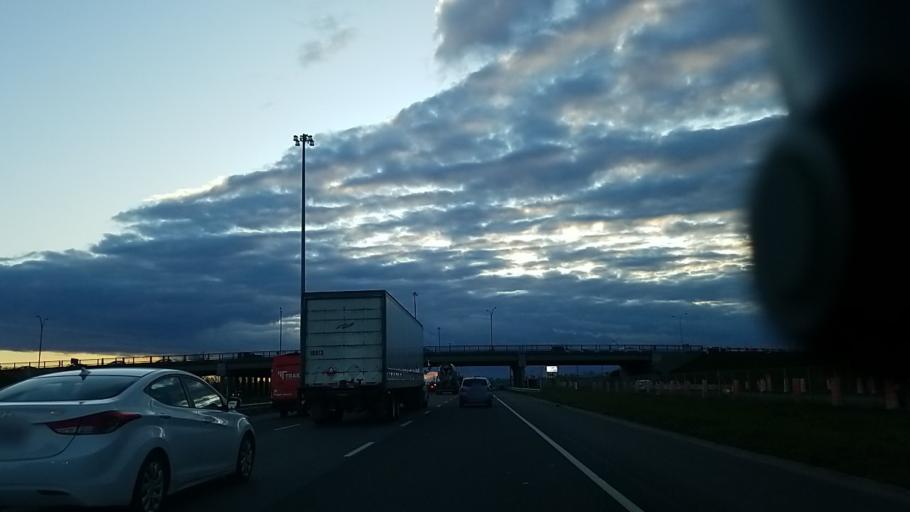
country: CA
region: Quebec
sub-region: Laurentides
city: Rosemere
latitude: 45.5648
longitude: -73.7749
